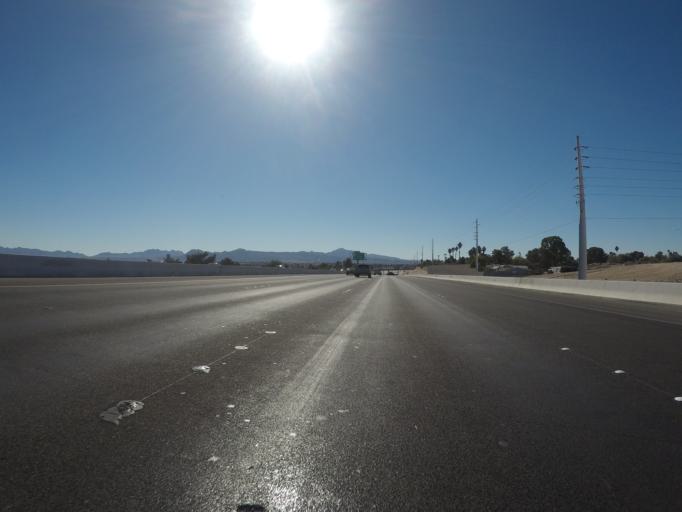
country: US
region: Nevada
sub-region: Clark County
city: Winchester
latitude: 36.1127
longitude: -115.0827
